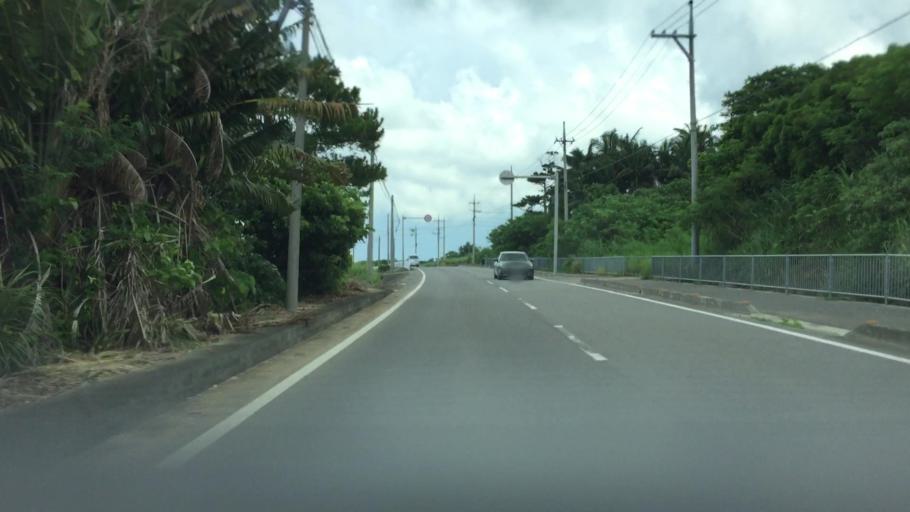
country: JP
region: Okinawa
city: Ishigaki
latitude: 24.3668
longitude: 124.1382
